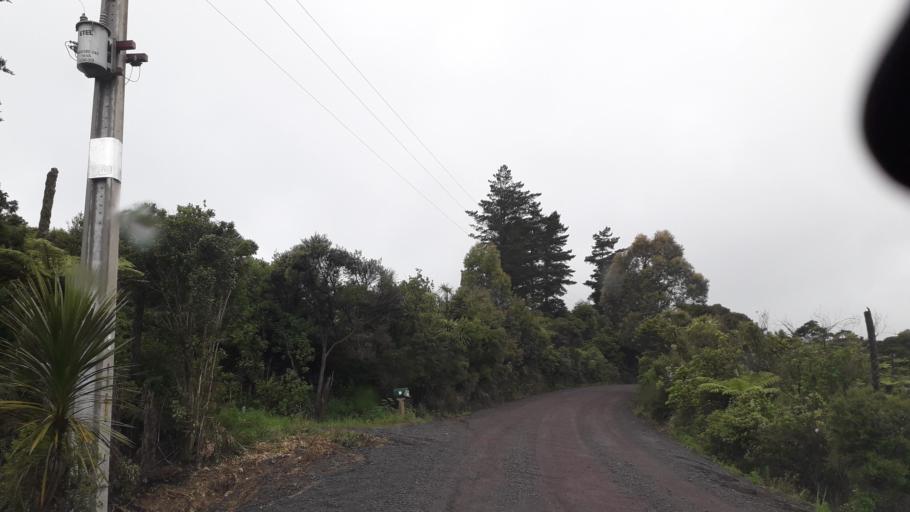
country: NZ
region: Northland
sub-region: Far North District
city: Paihia
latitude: -35.2381
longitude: 174.2502
